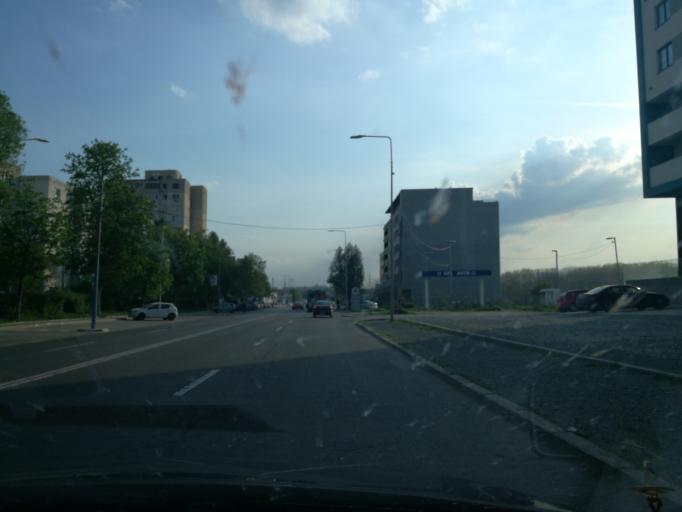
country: RO
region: Constanta
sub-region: Municipiul Constanta
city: Palazu Mare
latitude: 44.2107
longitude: 28.6192
